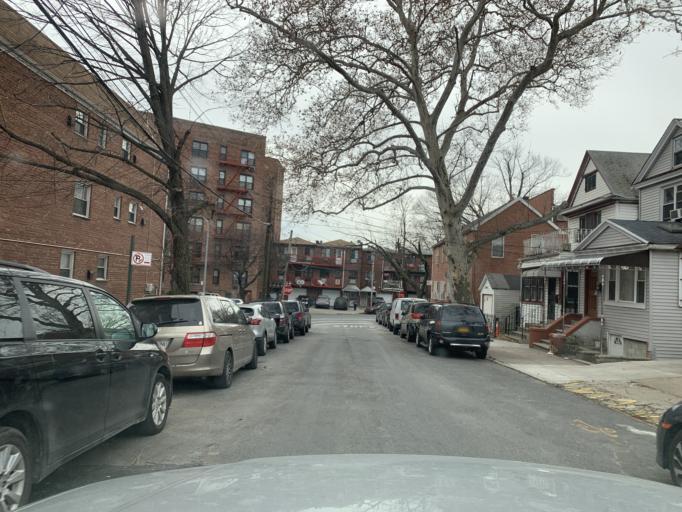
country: US
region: New York
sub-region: Queens County
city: Long Island City
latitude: 40.7409
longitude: -73.8868
